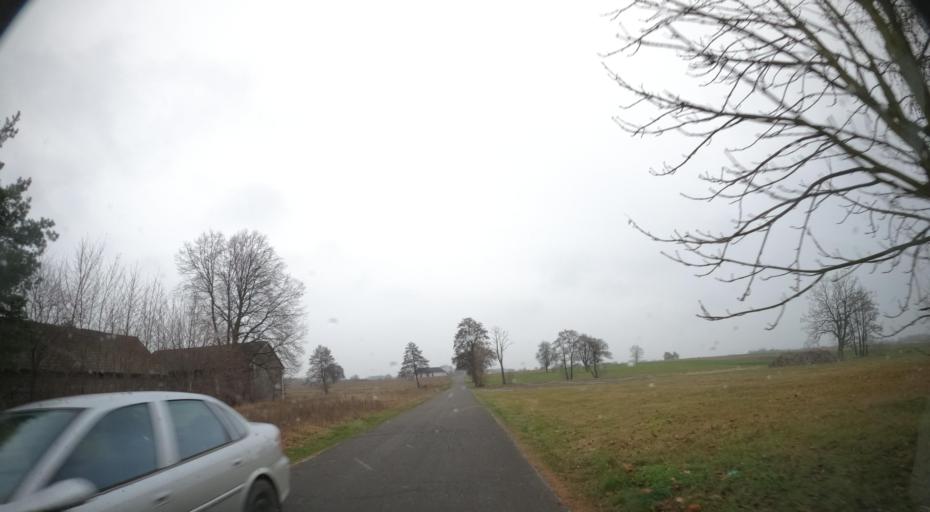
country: PL
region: Masovian Voivodeship
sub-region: Powiat radomski
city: Jedlnia-Letnisko
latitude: 51.4128
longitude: 21.2927
